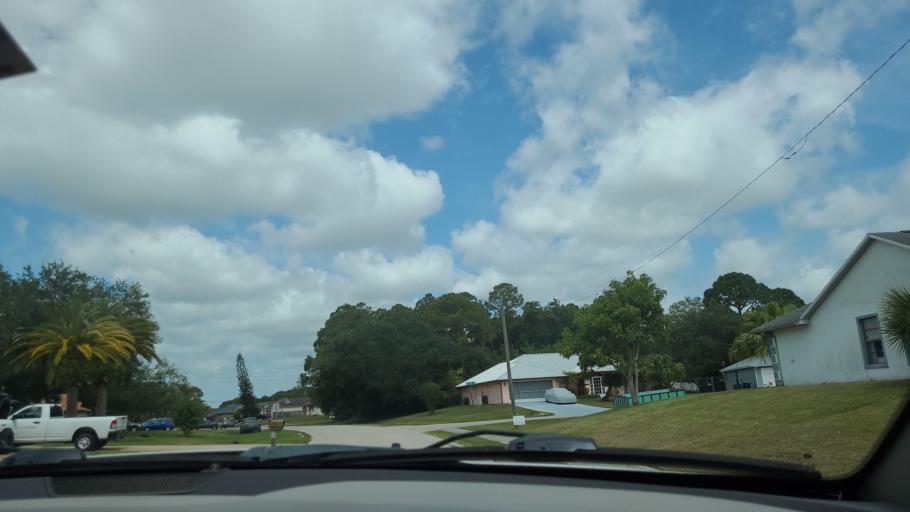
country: US
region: Florida
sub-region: Brevard County
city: Grant-Valkaria
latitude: 27.9674
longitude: -80.6595
